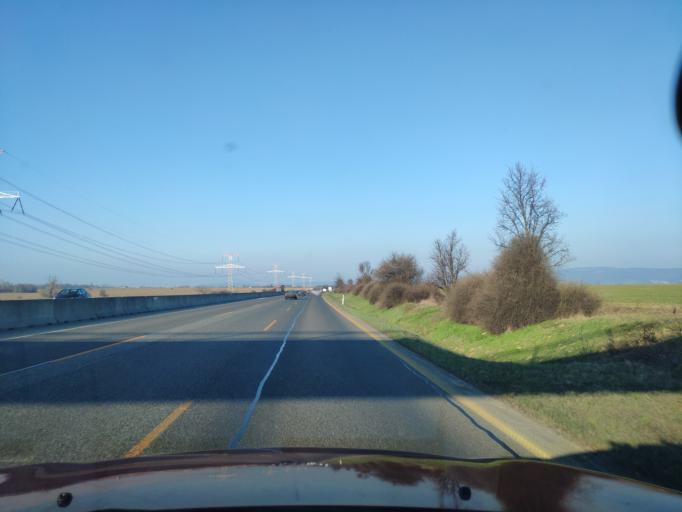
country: SK
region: Bratislavsky
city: Senec
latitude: 48.2150
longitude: 17.3130
